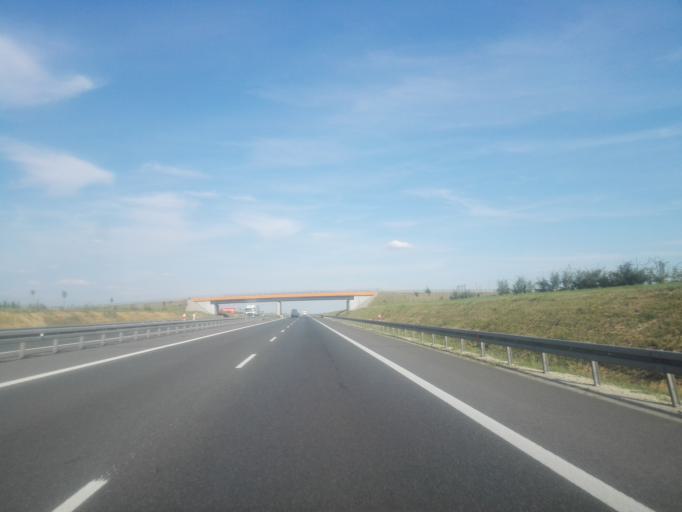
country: PL
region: Lower Silesian Voivodeship
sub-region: Powiat olesnicki
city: Dobroszyce
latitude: 51.2271
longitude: 17.2685
